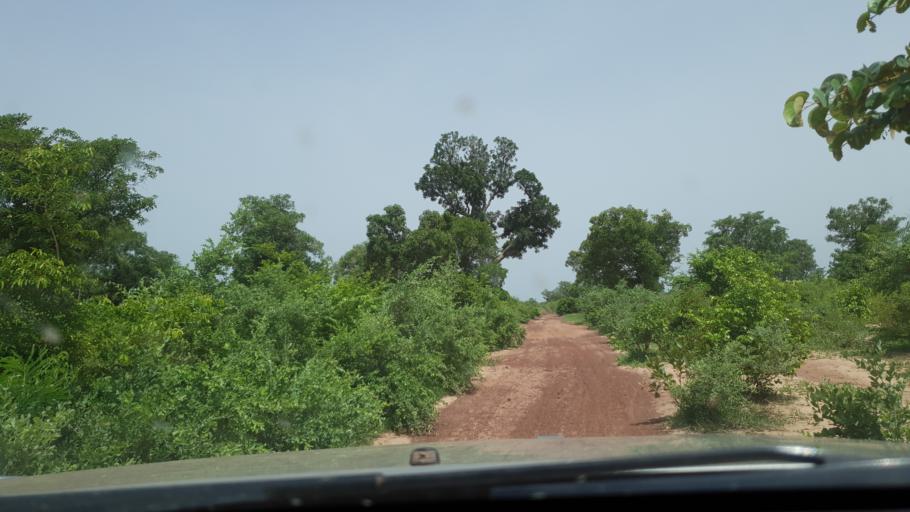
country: ML
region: Koulikoro
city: Koulikoro
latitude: 12.6647
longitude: -7.2175
